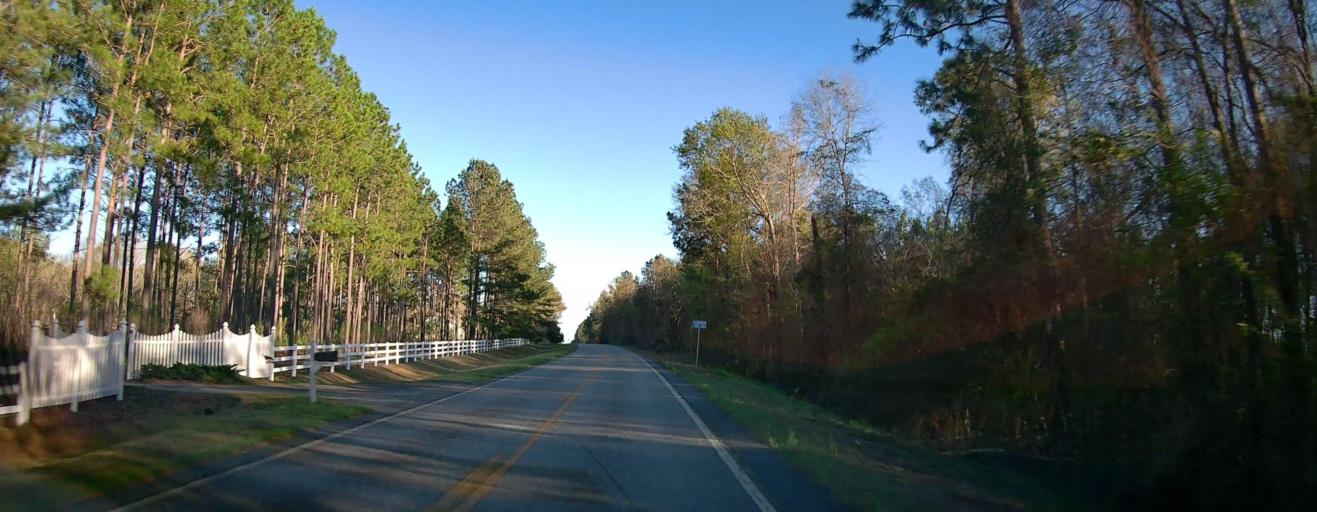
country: US
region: Georgia
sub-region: Wilcox County
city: Abbeville
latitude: 32.1111
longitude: -83.3179
